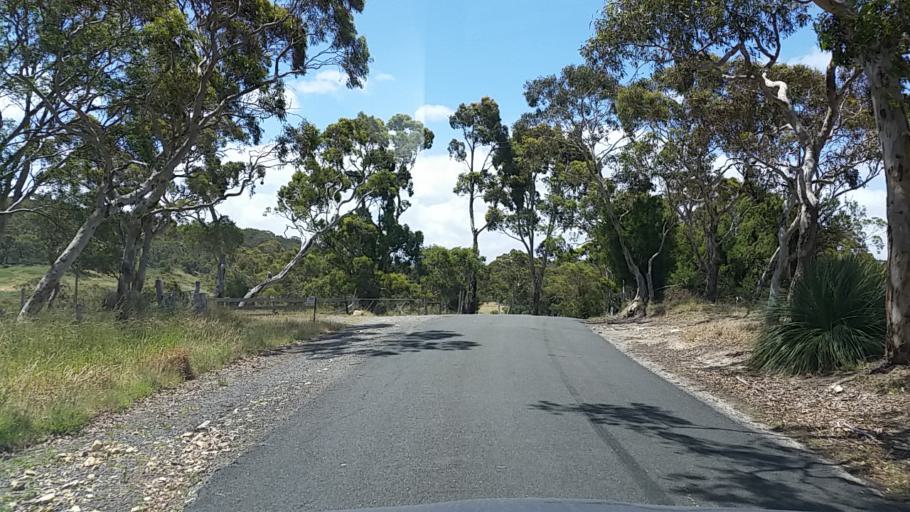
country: AU
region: South Australia
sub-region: Alexandrina
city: Mount Compass
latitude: -35.4466
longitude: 138.5919
